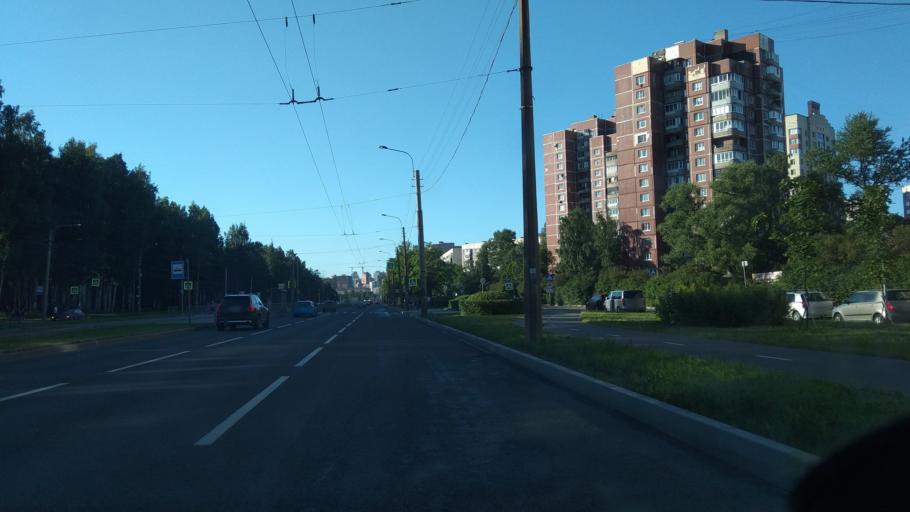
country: RU
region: St.-Petersburg
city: Sosnovka
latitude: 60.0247
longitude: 30.3665
